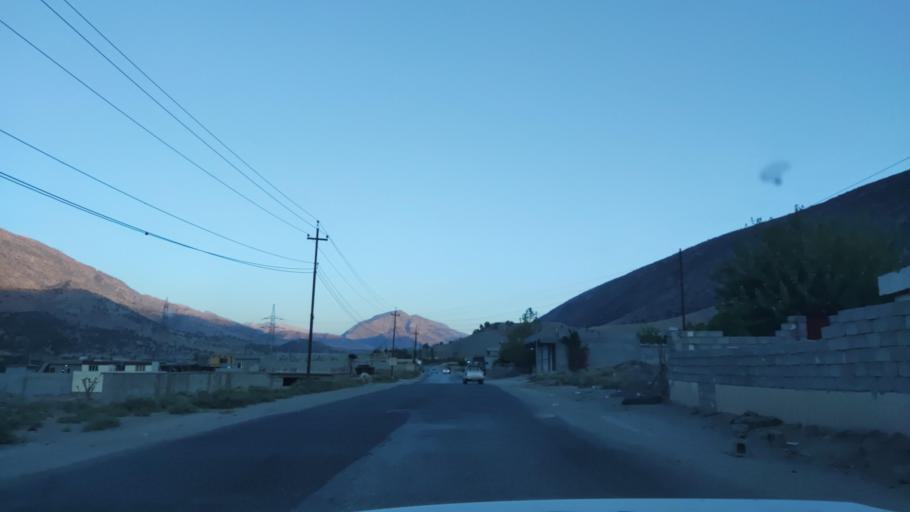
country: IQ
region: Arbil
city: Ruwandiz
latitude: 36.5874
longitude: 44.3947
